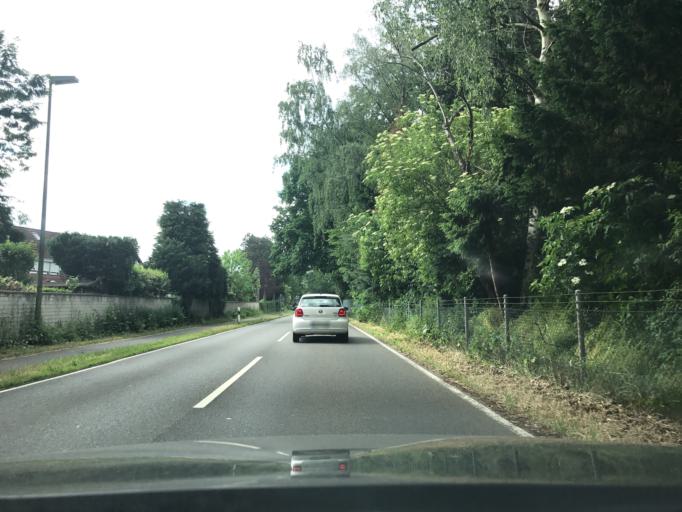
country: DE
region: North Rhine-Westphalia
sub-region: Regierungsbezirk Dusseldorf
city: Meerbusch
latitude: 51.2902
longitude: 6.6506
